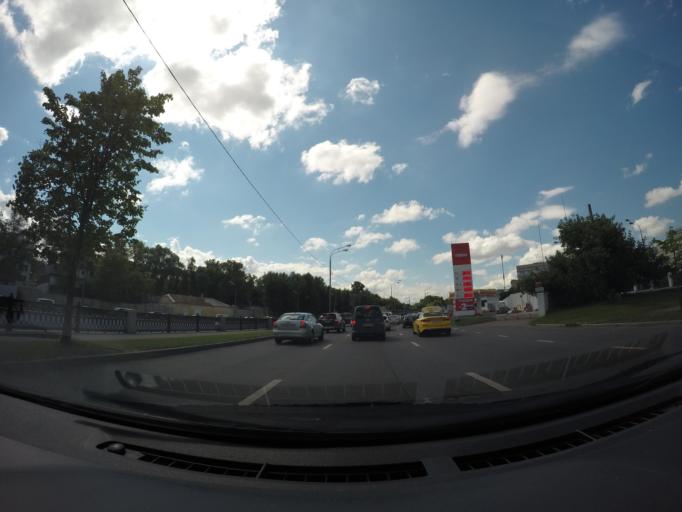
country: RU
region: Moscow
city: Lefortovo
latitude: 55.7709
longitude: 37.6937
